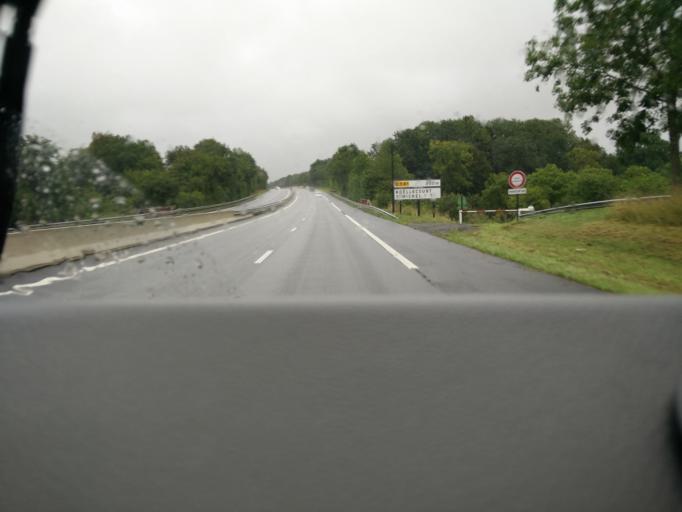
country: FR
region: Nord-Pas-de-Calais
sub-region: Departement du Pas-de-Calais
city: Saint-Pol-sur-Ternoise
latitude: 50.3634
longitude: 2.3875
